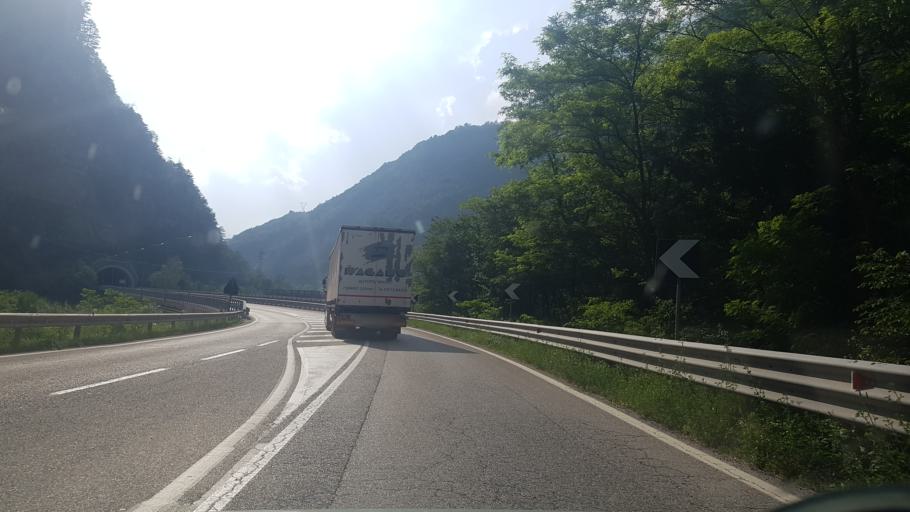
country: IT
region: Friuli Venezia Giulia
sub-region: Provincia di Udine
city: Chiusaforte
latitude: 46.3956
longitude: 13.2722
